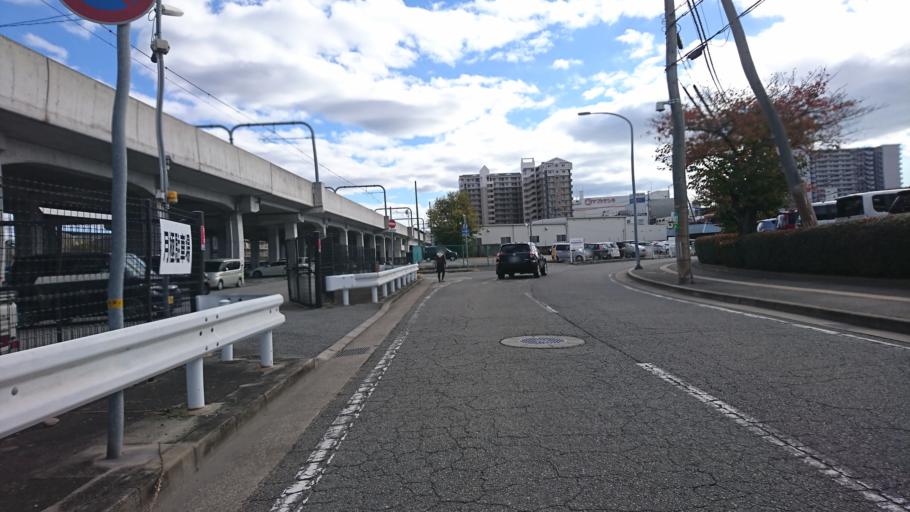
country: JP
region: Hyogo
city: Kakogawacho-honmachi
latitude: 34.7698
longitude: 134.8370
